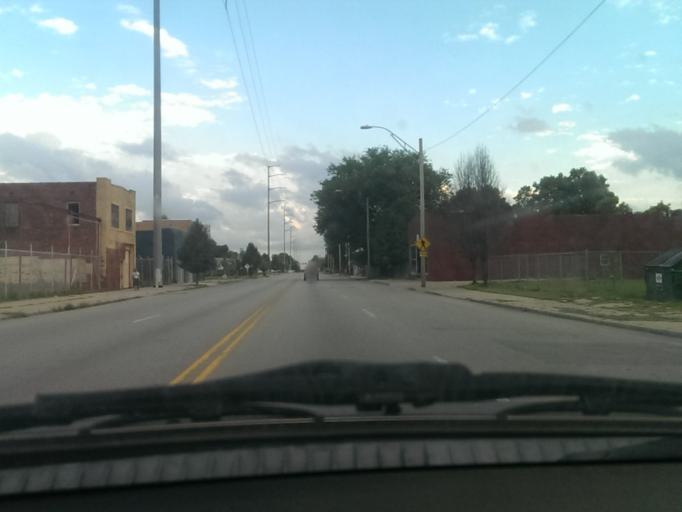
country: US
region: Missouri
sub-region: Jackson County
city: Kansas City
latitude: 39.0607
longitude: -94.5719
